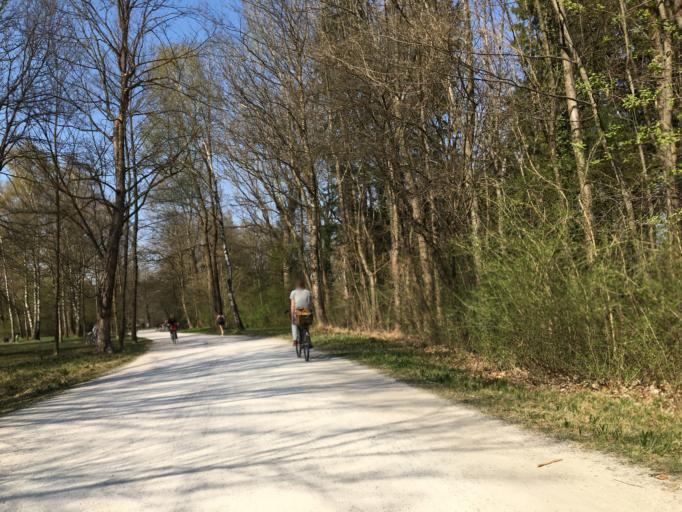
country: DE
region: Bavaria
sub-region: Upper Bavaria
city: Bogenhausen
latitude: 48.1733
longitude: 11.6181
